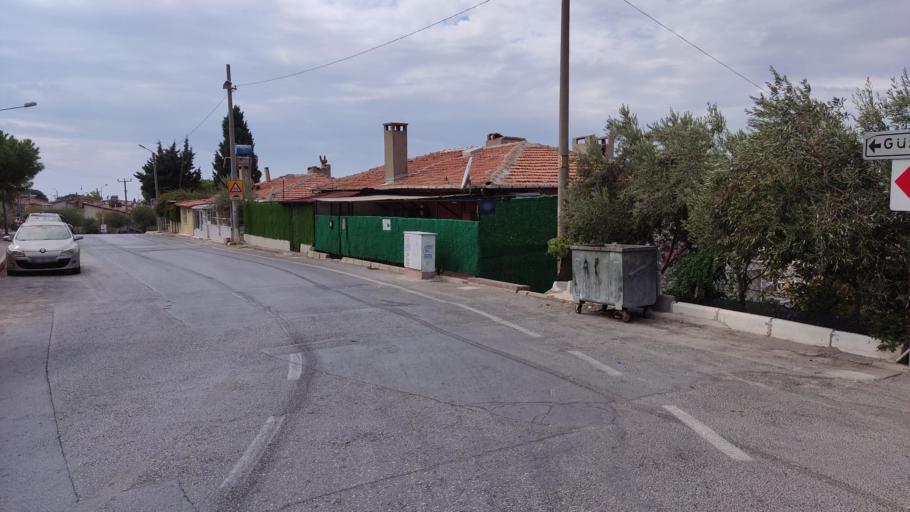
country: TR
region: Izmir
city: Karsiyaka
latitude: 38.5011
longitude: 27.0849
